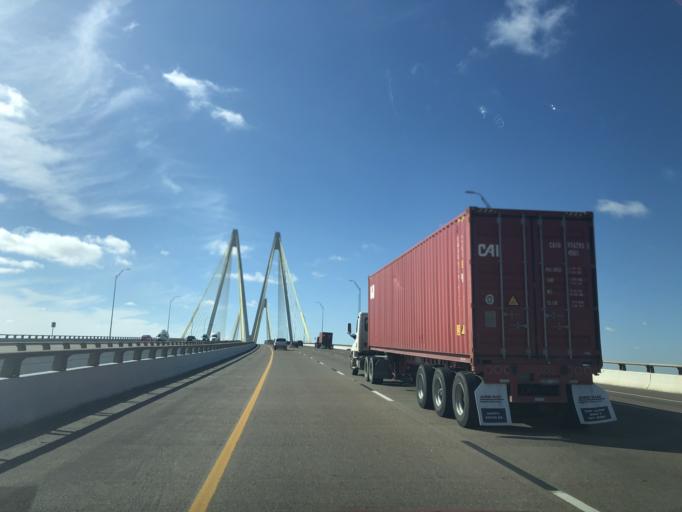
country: US
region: Texas
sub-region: Harris County
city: La Porte
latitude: 29.7076
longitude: -95.0121
